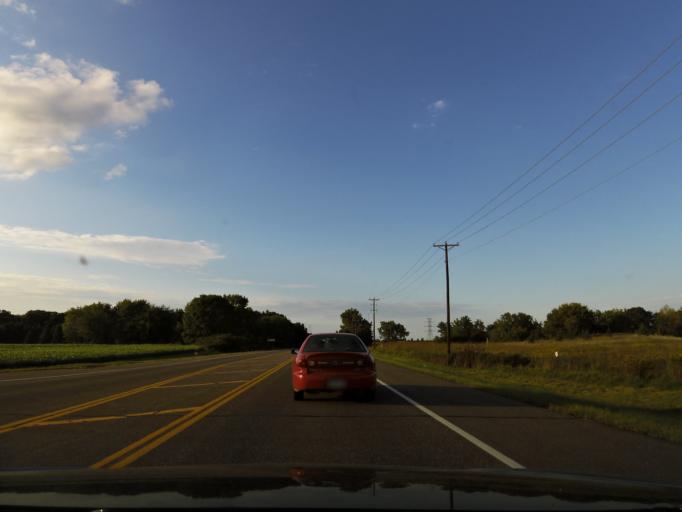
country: US
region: Minnesota
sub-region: Washington County
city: Cottage Grove
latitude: 44.8205
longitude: -92.9036
